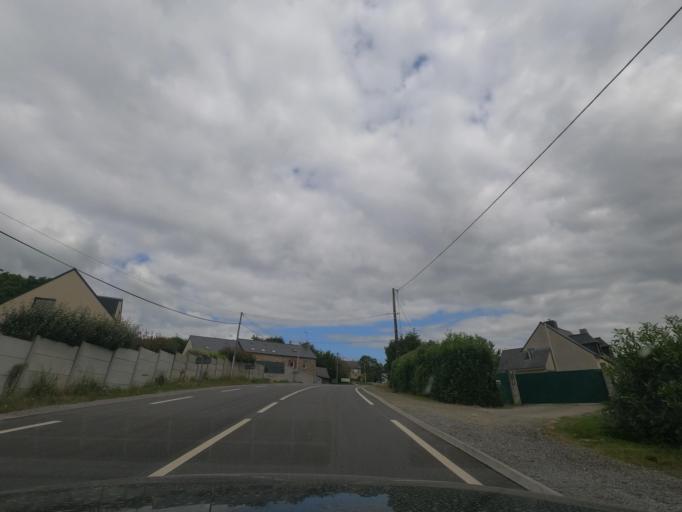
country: FR
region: Brittany
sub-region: Departement d'Ille-et-Vilaine
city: Saint-Jean-sur-Couesnon
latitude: 48.3029
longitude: -1.3564
